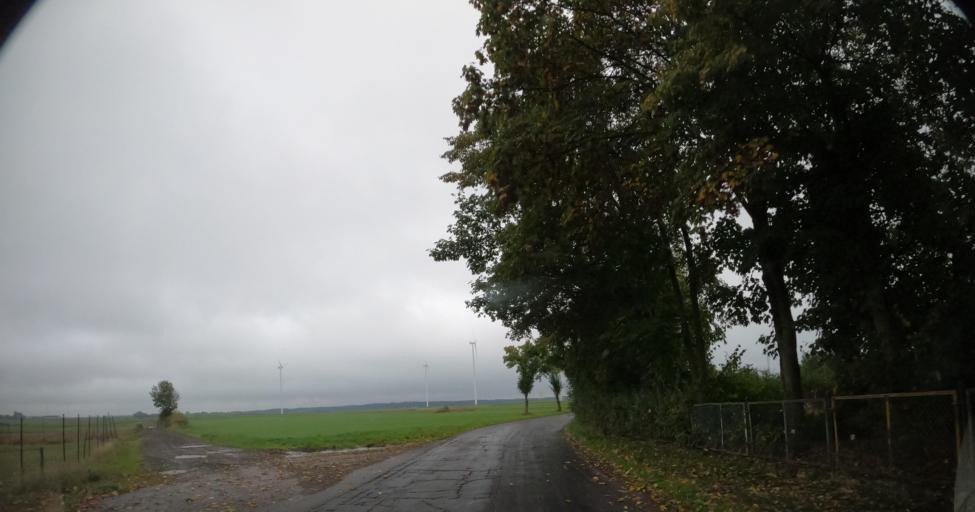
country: PL
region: West Pomeranian Voivodeship
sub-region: Powiat pyrzycki
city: Kozielice
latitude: 53.0892
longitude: 14.7734
